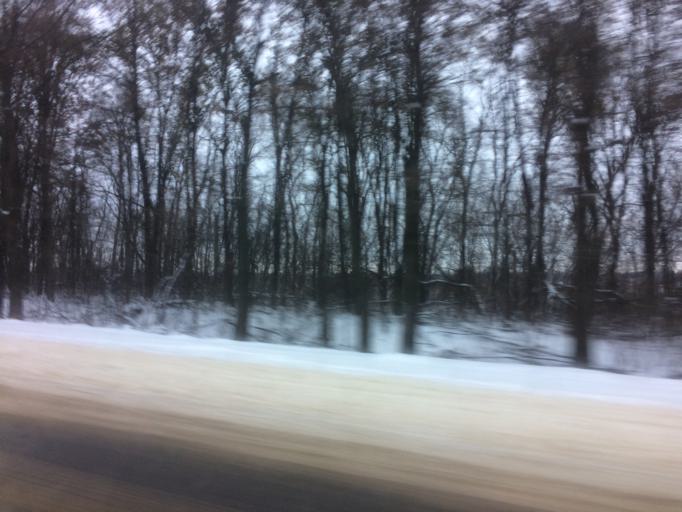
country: RU
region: Tula
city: Tula
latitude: 54.1508
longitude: 37.6404
